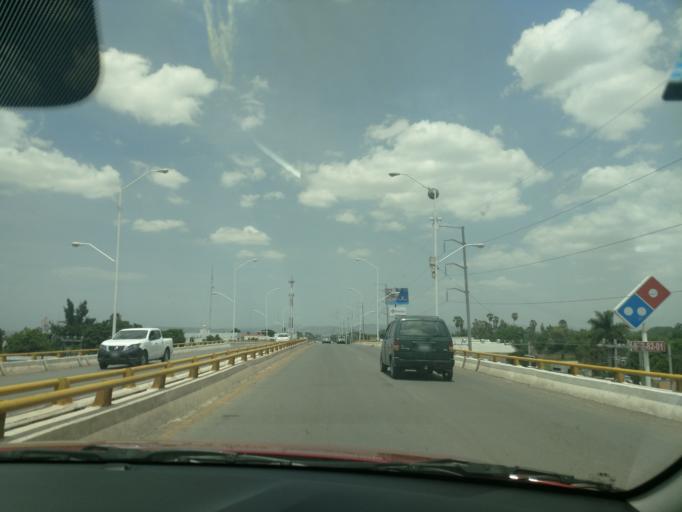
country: MX
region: San Luis Potosi
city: Rio Verde
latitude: 21.9232
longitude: -99.9940
